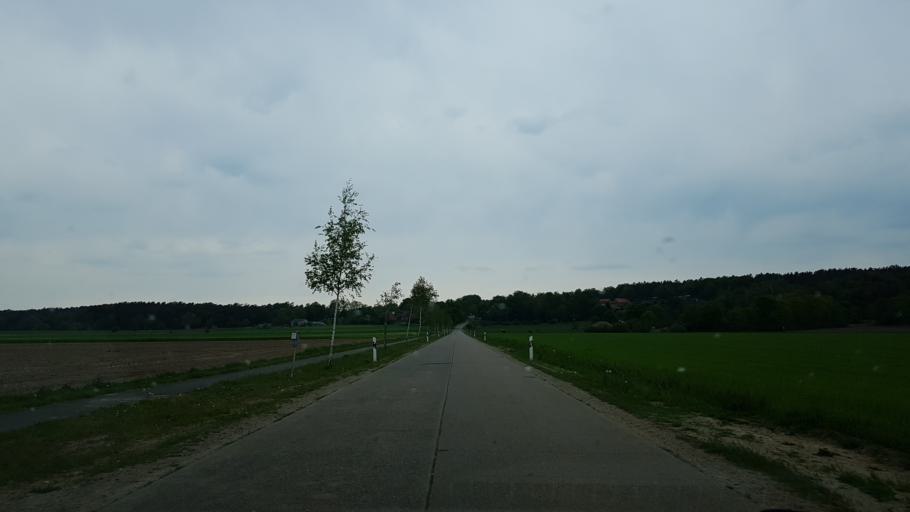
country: DE
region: Lower Saxony
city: Gartow
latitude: 53.0480
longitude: 11.4398
